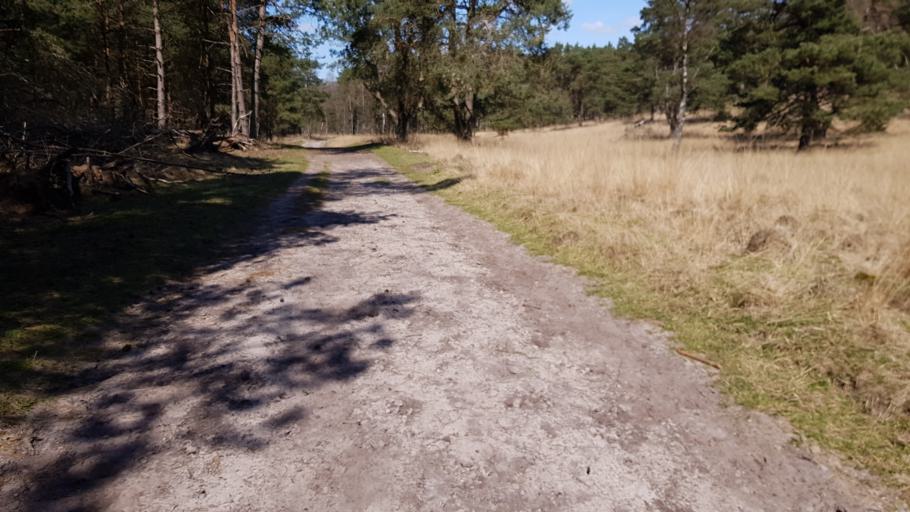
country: NL
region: Gelderland
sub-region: Gemeente Rheden
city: Rheden
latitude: 52.0596
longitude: 6.0057
